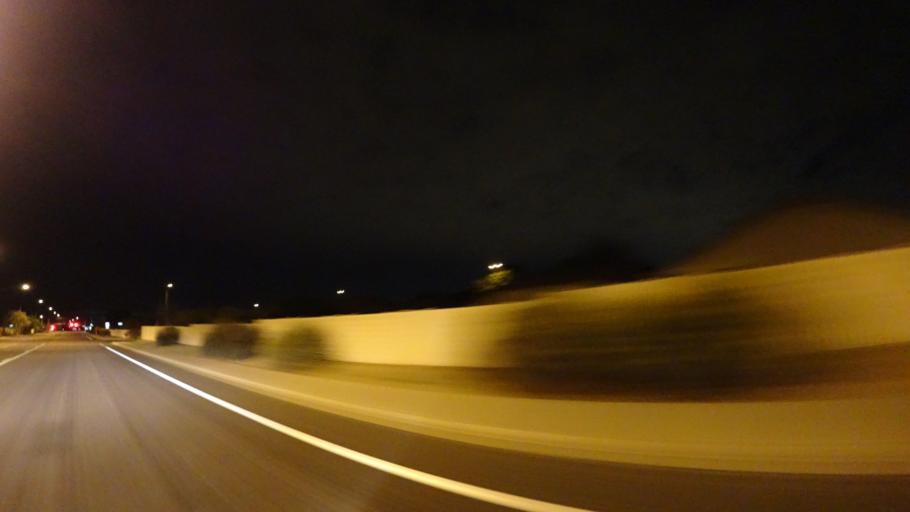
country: US
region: Arizona
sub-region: Pinal County
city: Apache Junction
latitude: 33.4261
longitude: -111.6587
